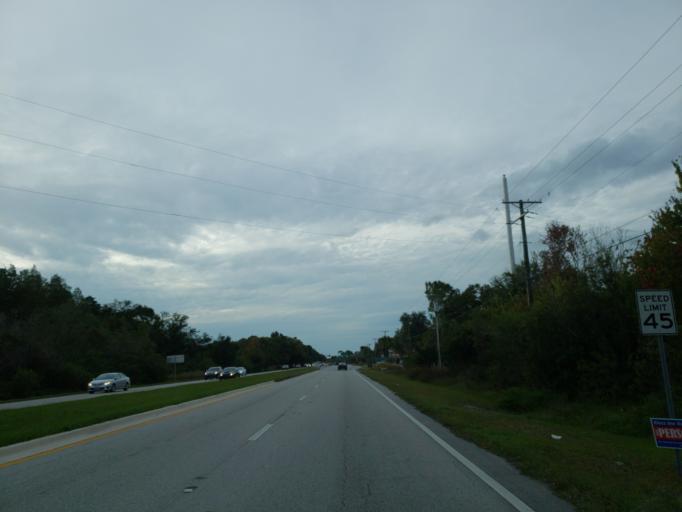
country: US
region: Florida
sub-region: Hillsborough County
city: Carrollwood Village
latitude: 28.0574
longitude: -82.5323
